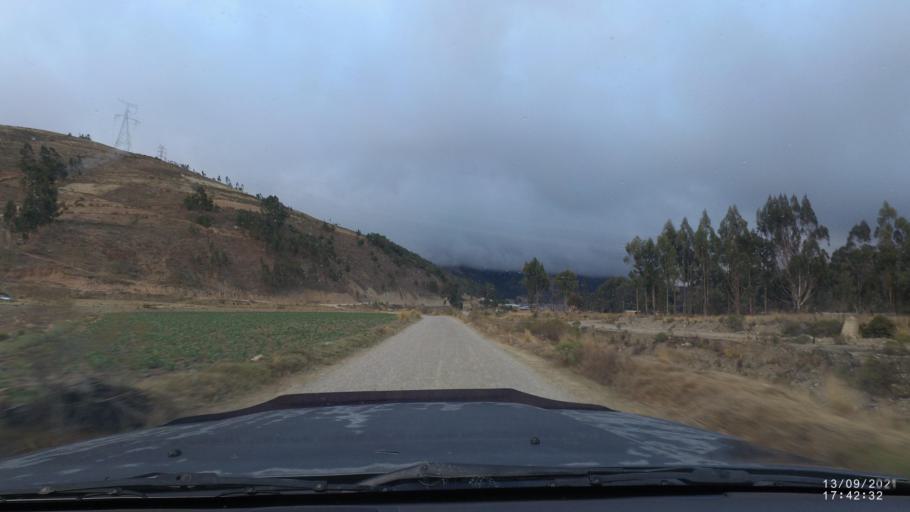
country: BO
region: Cochabamba
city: Colomi
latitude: -17.3698
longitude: -65.8174
